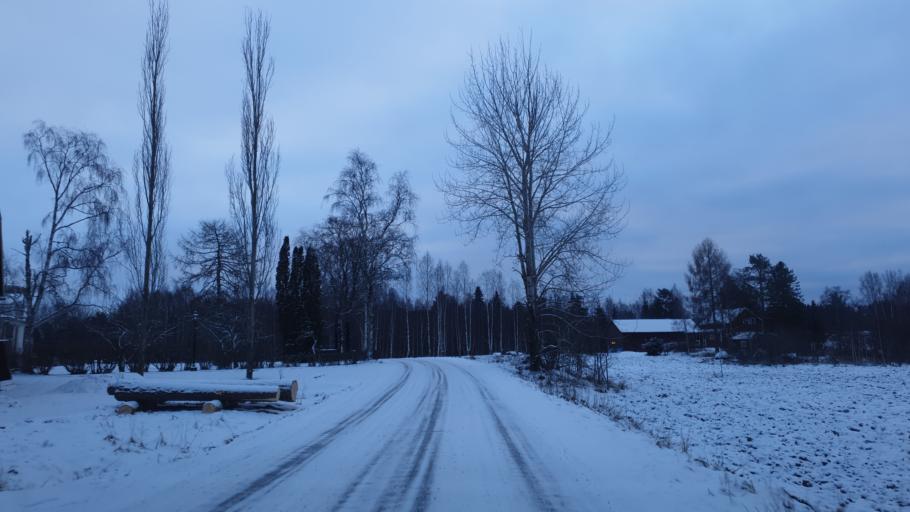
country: SE
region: Gaevleborg
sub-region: Bollnas Kommun
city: Kilafors
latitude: 61.2537
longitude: 16.5441
